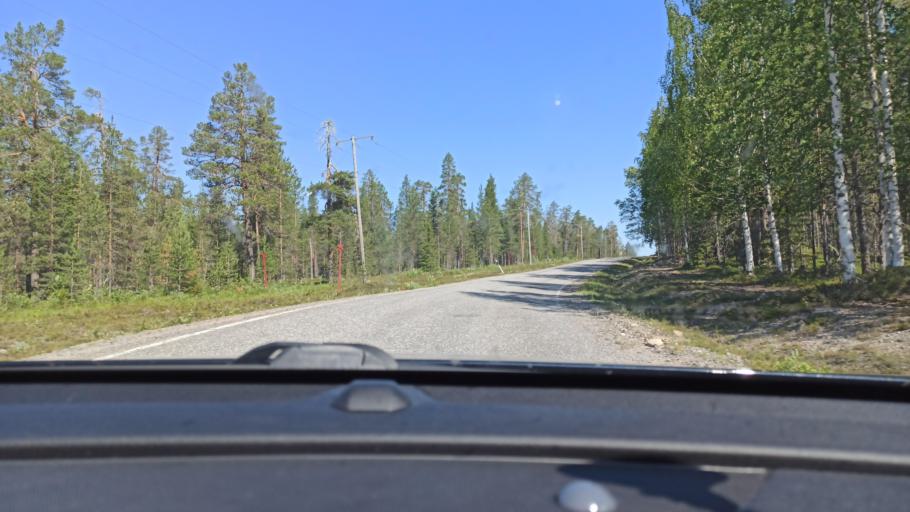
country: FI
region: Lapland
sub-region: Tunturi-Lappi
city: Kolari
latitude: 67.6371
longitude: 24.1564
